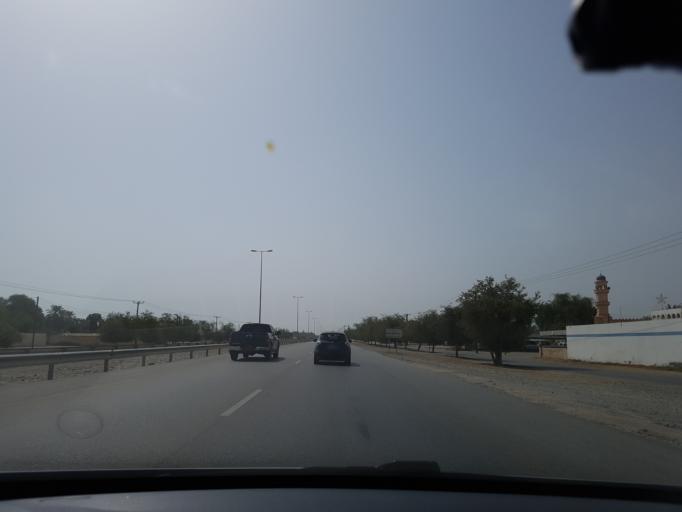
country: OM
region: Al Batinah
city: Al Khaburah
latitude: 23.9904
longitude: 57.0711
